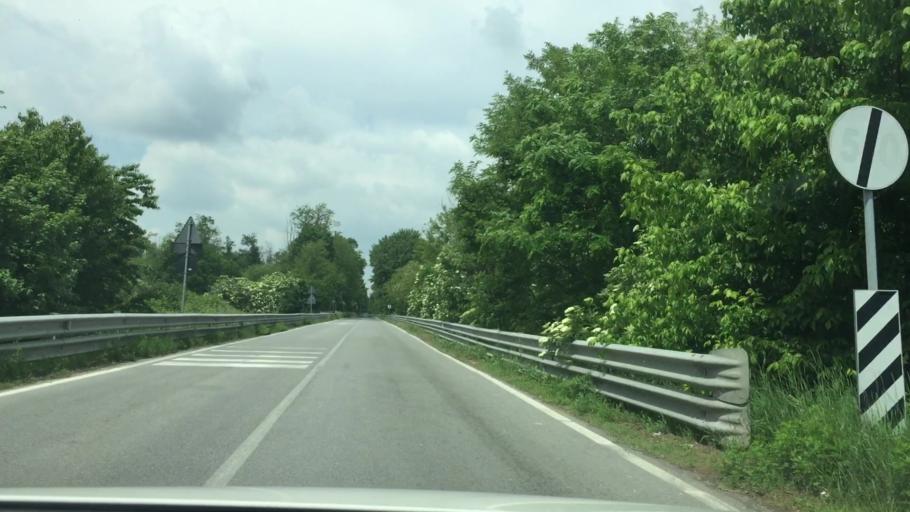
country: IT
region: Lombardy
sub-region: Provincia di Varese
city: Lonate Pozzolo
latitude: 45.5654
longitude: 8.7508
